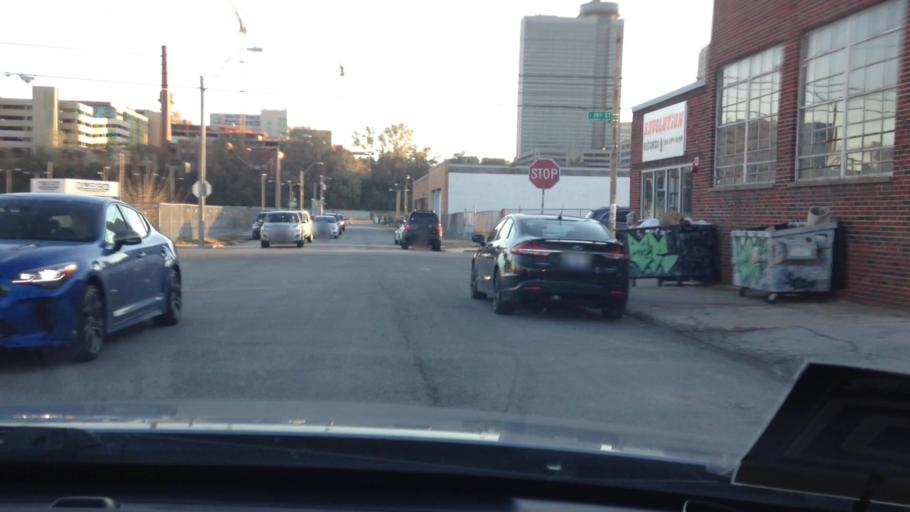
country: US
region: Missouri
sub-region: Jackson County
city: Kansas City
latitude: 39.0906
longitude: -94.5779
